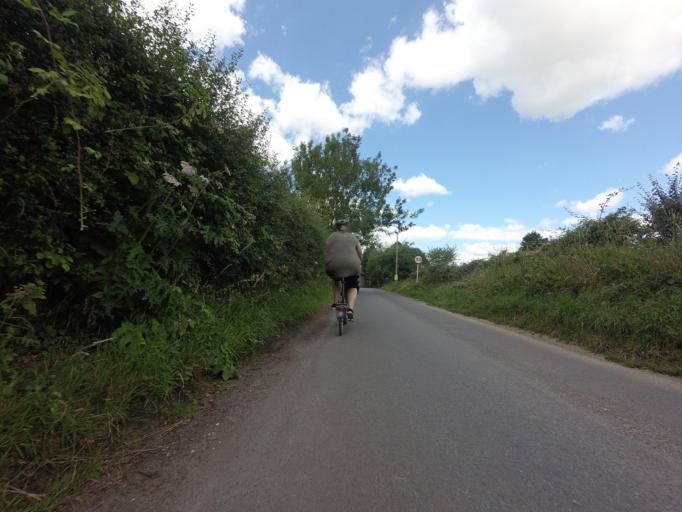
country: GB
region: England
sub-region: East Sussex
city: Ringmer
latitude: 50.8684
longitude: 0.1512
